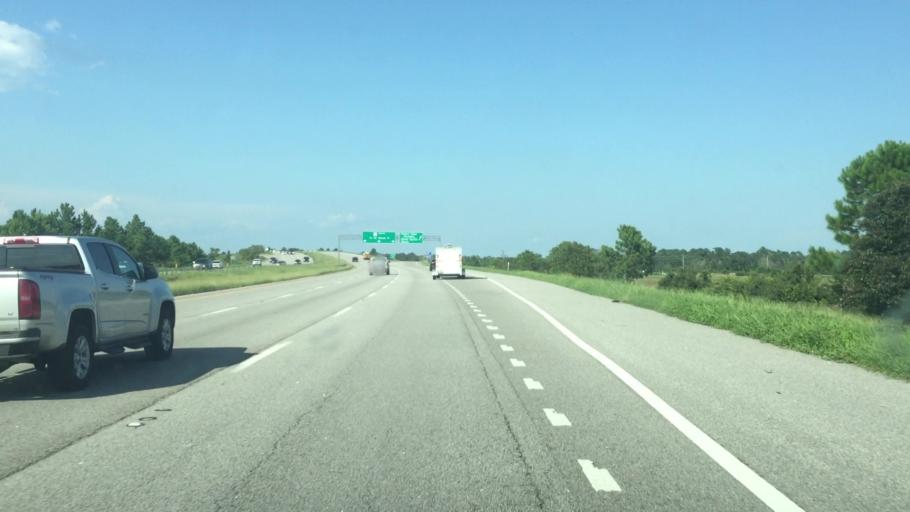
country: US
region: South Carolina
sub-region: Horry County
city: North Myrtle Beach
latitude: 33.8386
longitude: -78.7059
